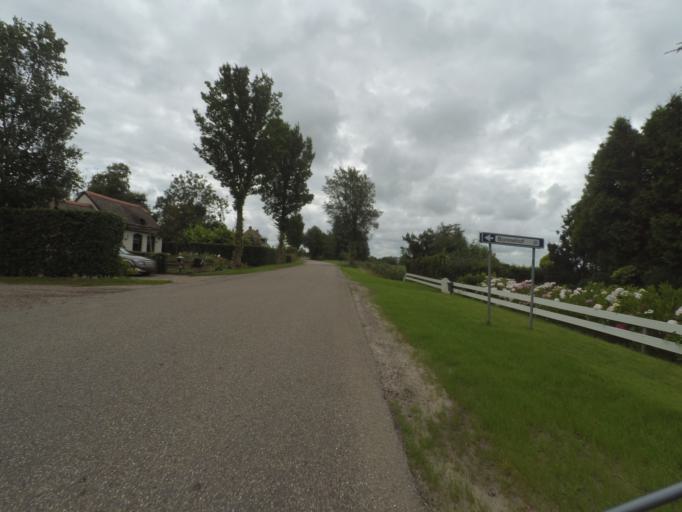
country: NL
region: Friesland
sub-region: Gemeente Kollumerland en Nieuwkruisland
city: Kollumerzwaag
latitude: 53.3083
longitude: 6.0893
